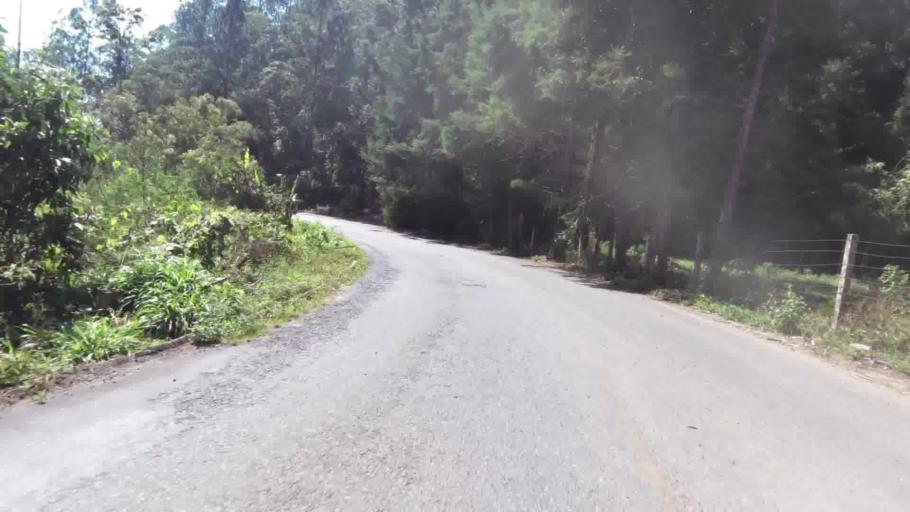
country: BR
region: Espirito Santo
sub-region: Marechal Floriano
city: Marechal Floriano
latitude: -20.4480
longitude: -40.8882
